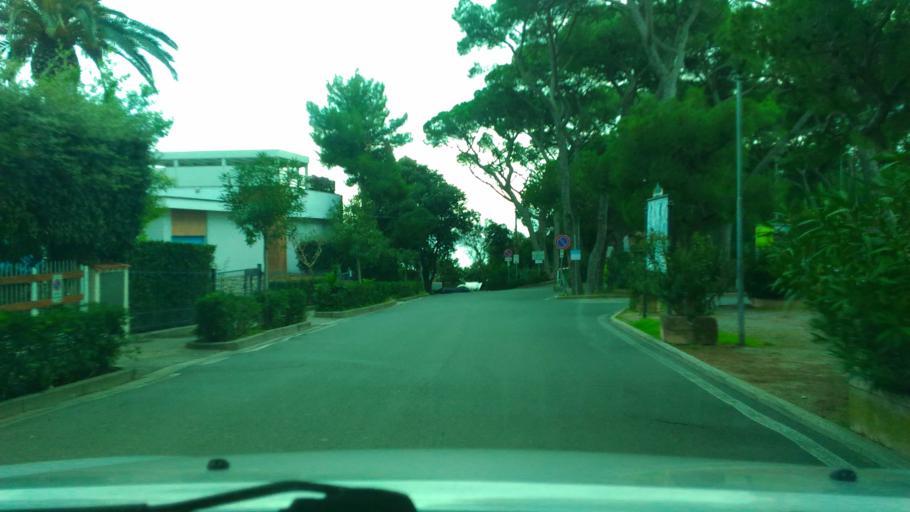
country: IT
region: Tuscany
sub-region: Provincia di Livorno
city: Rosignano Solvay-Castiglioncello
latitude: 43.4043
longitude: 10.4160
